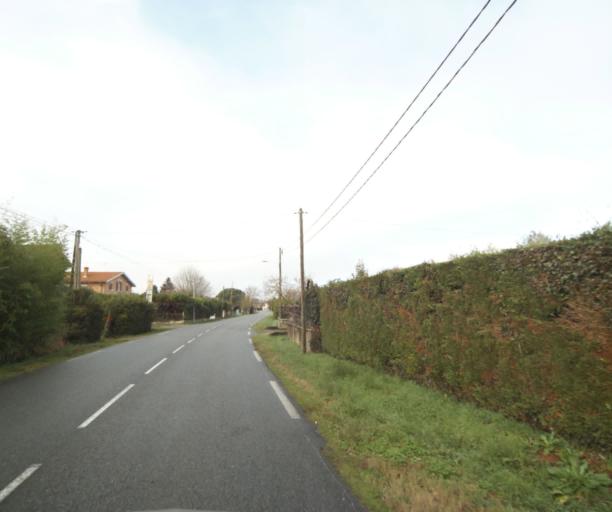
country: FR
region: Midi-Pyrenees
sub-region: Departement de la Haute-Garonne
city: Villemur-sur-Tarn
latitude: 43.8596
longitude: 1.4924
